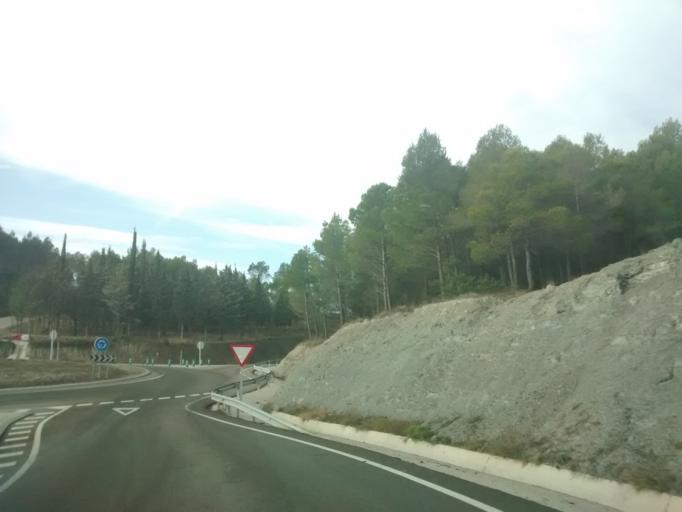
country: ES
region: Aragon
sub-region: Provincia de Zaragoza
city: Undues de Lerda
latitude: 42.6177
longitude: -1.1142
